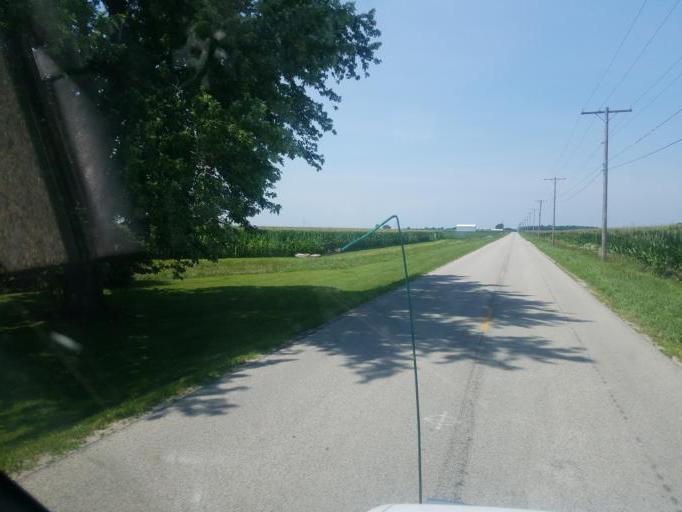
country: US
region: Ohio
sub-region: Shelby County
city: Sidney
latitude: 40.3037
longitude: -84.0682
